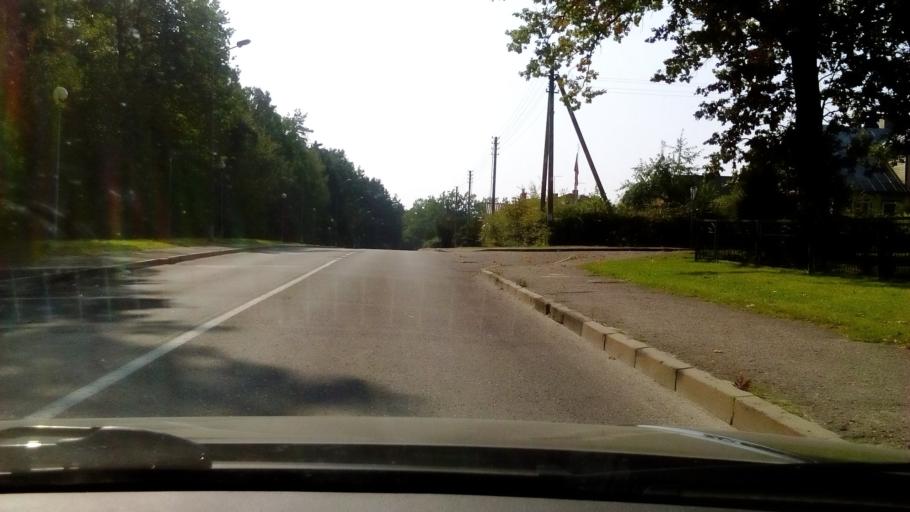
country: LT
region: Alytaus apskritis
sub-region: Alytus
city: Alytus
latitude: 54.3867
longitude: 24.0628
